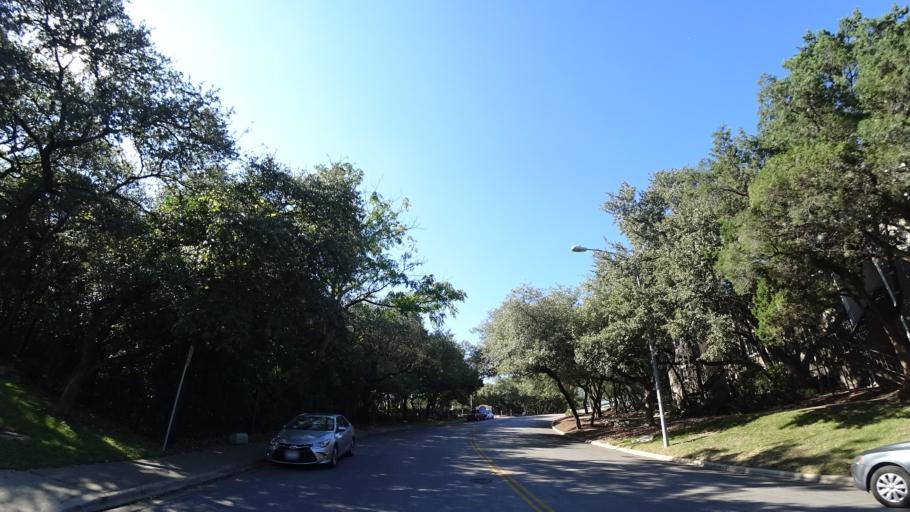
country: US
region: Texas
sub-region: Travis County
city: Rollingwood
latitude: 30.2581
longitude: -97.7904
